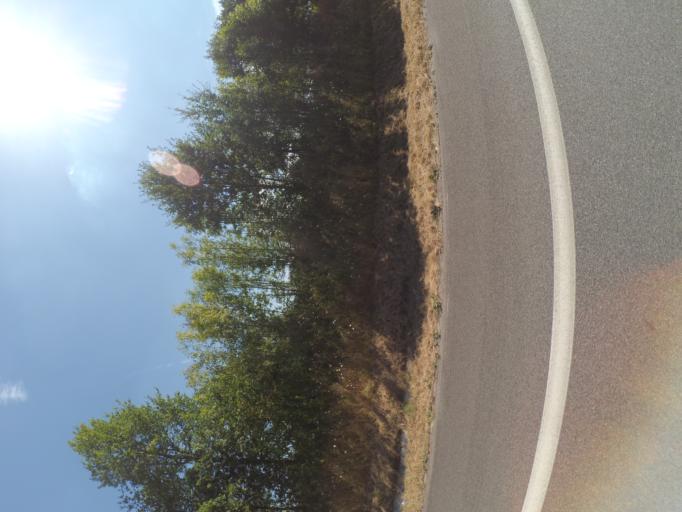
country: FR
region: Limousin
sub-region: Departement de la Haute-Vienne
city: Saint-Victurnien
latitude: 45.8901
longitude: 1.0529
